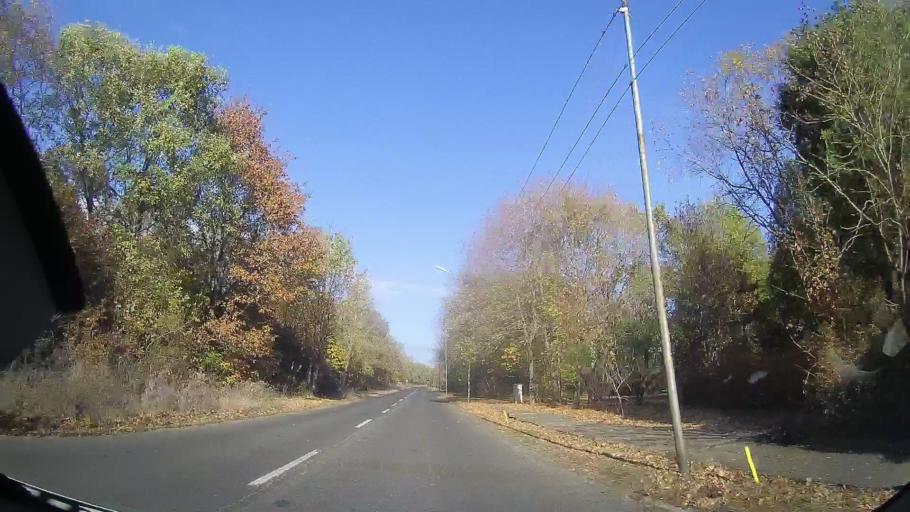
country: RO
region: Constanta
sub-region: Comuna Douazeci si Trei August
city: Douazeci si Trei August
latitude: 43.8714
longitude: 28.5955
